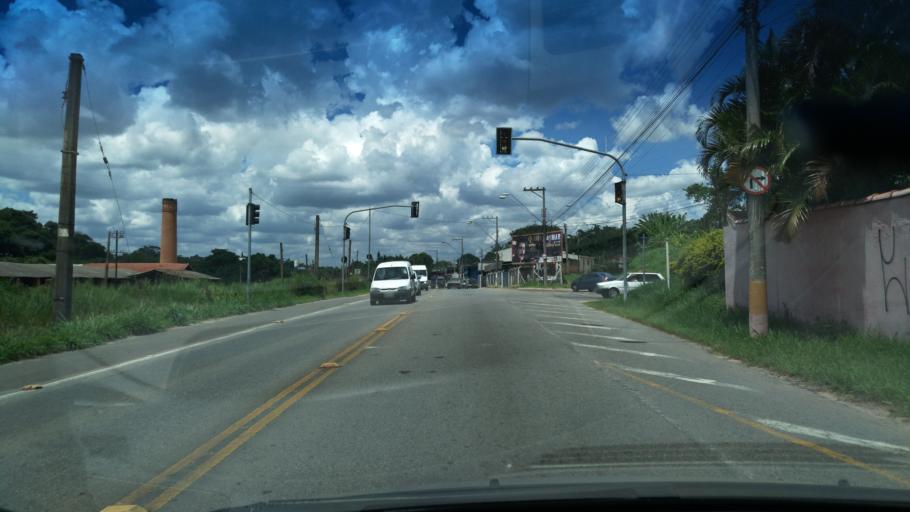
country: BR
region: Sao Paulo
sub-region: Vinhedo
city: Vinhedo
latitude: -23.0031
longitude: -46.9883
